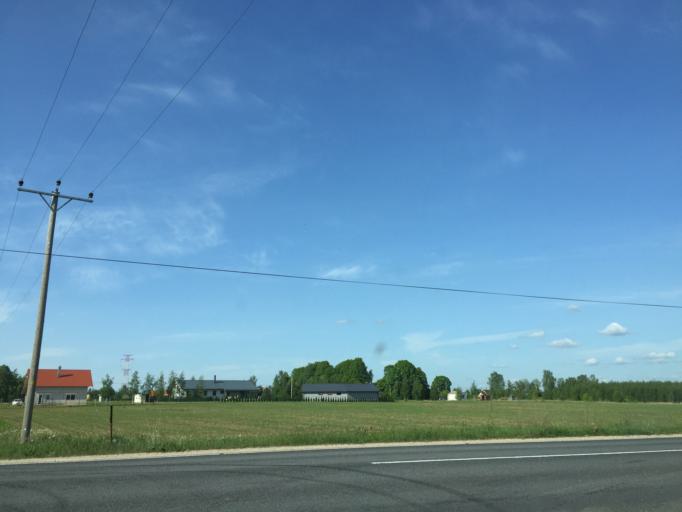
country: LV
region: Salaspils
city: Salaspils
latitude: 56.8255
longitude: 24.3671
